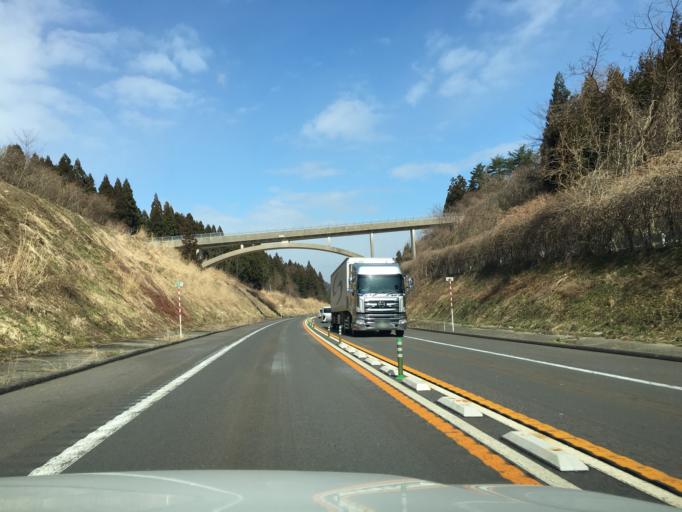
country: JP
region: Akita
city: Akita
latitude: 39.7671
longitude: 140.1227
